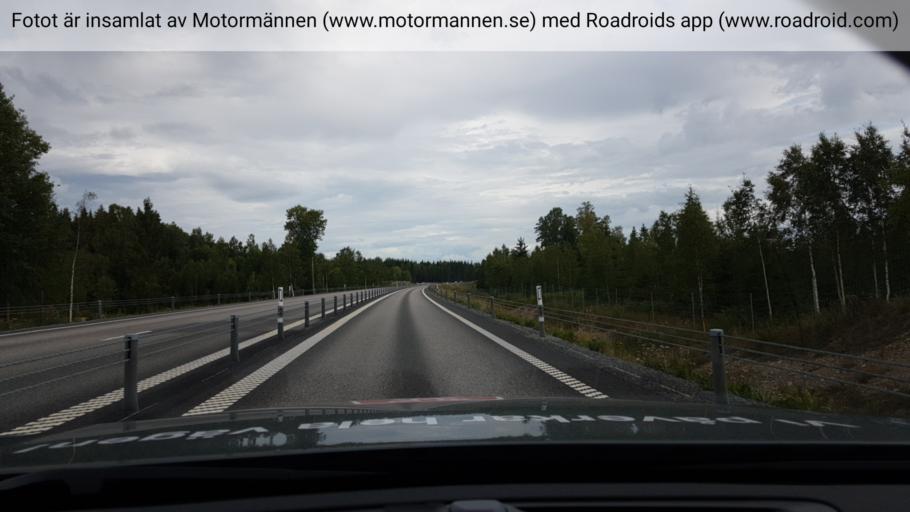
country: SE
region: Uppsala
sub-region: Heby Kommun
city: Heby
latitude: 60.0061
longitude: 16.8516
